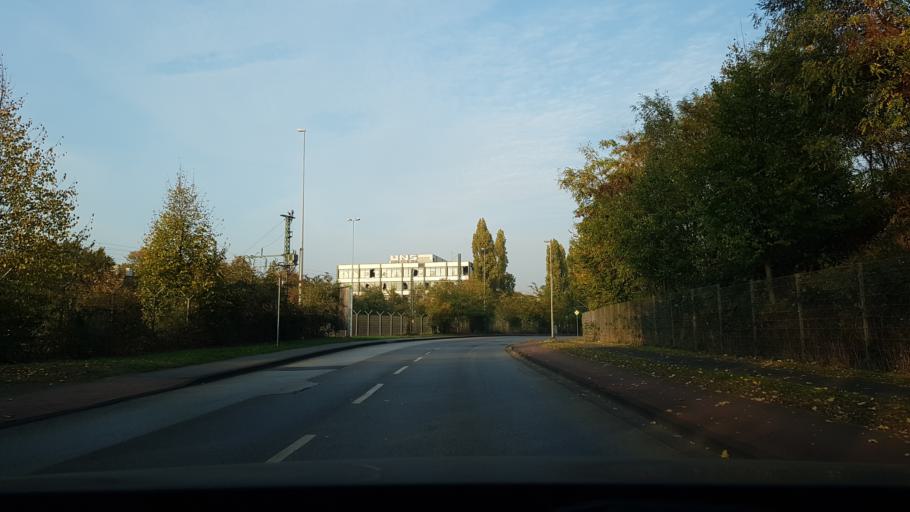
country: DE
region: North Rhine-Westphalia
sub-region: Regierungsbezirk Dusseldorf
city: Hochfeld
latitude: 51.3986
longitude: 6.7188
